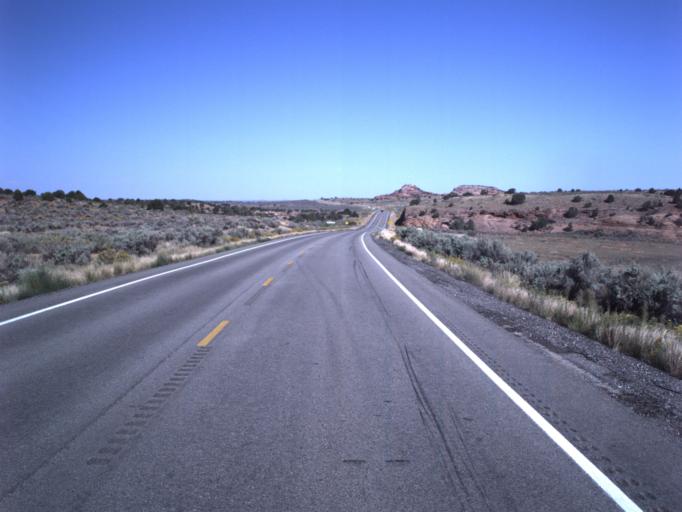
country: US
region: Utah
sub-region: Grand County
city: Moab
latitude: 38.3020
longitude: -109.3951
